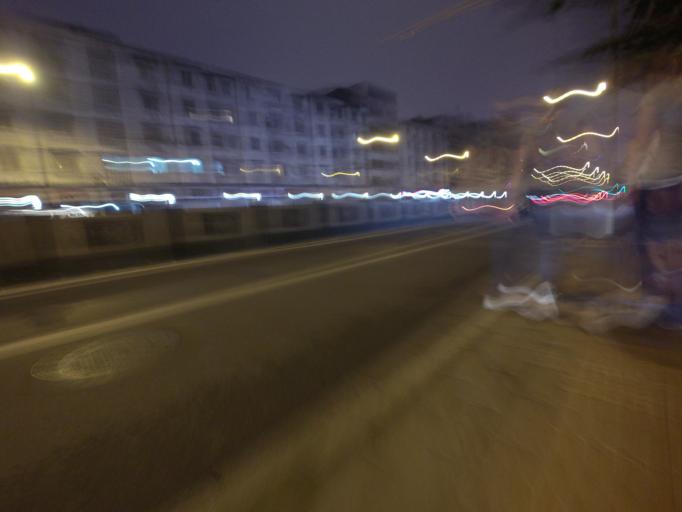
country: CN
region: Sichuan
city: Chengdu
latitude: 30.6685
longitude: 104.0581
